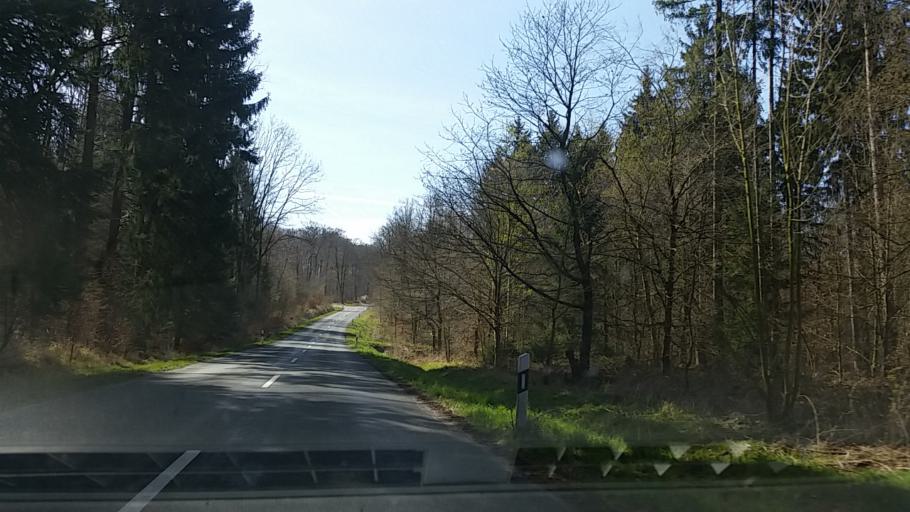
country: DE
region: Lower Saxony
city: Rabke
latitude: 52.1700
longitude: 10.8571
